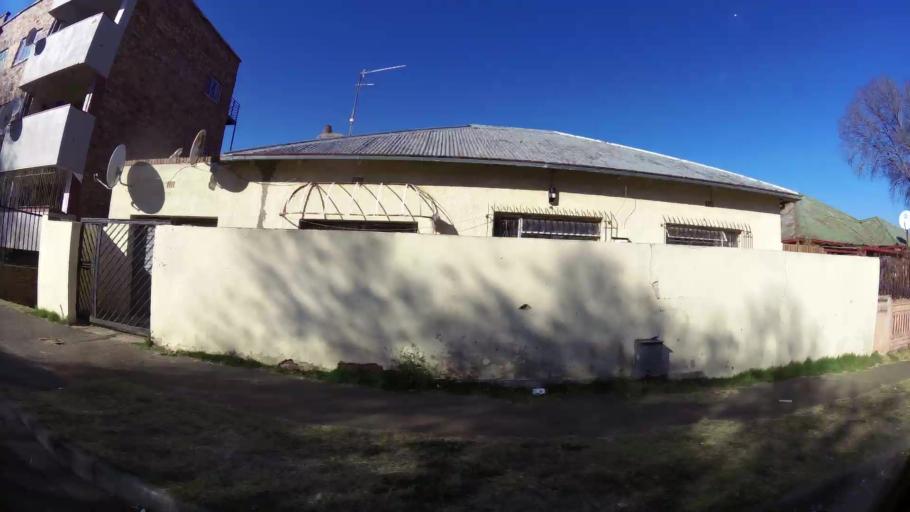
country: ZA
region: Gauteng
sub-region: City of Johannesburg Metropolitan Municipality
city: Johannesburg
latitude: -26.2036
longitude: 28.0889
